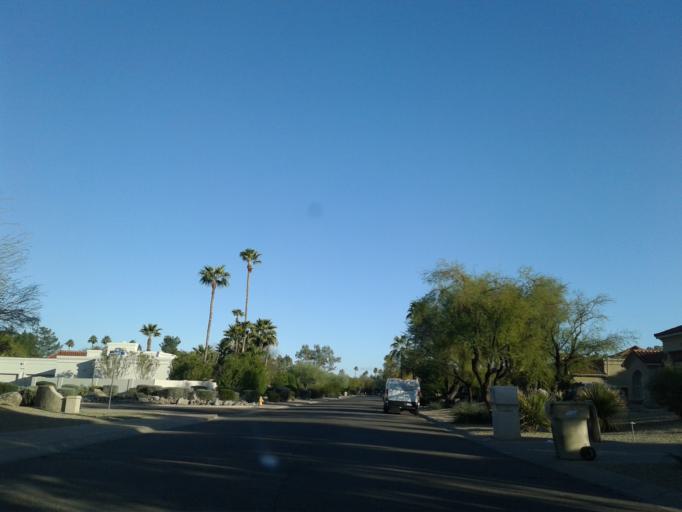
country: US
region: Arizona
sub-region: Maricopa County
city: Paradise Valley
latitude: 33.5706
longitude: -111.9558
